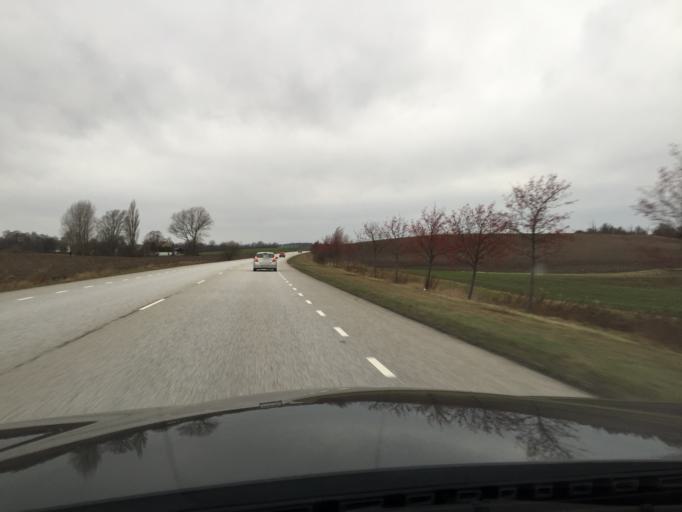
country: SE
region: Skane
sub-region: Malmo
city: Oxie
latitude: 55.5844
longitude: 13.1302
